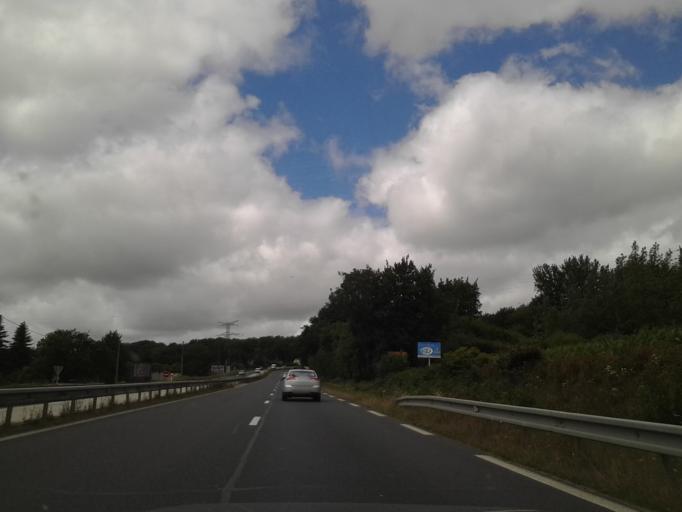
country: FR
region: Lower Normandy
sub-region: Departement de la Manche
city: Brix
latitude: 49.5451
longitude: -1.5547
